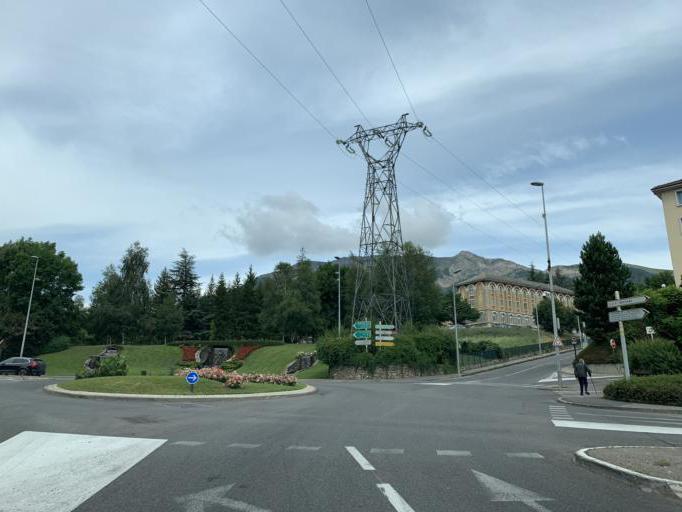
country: FR
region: Provence-Alpes-Cote d'Azur
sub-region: Departement des Hautes-Alpes
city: Gap
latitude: 44.5579
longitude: 6.0690
